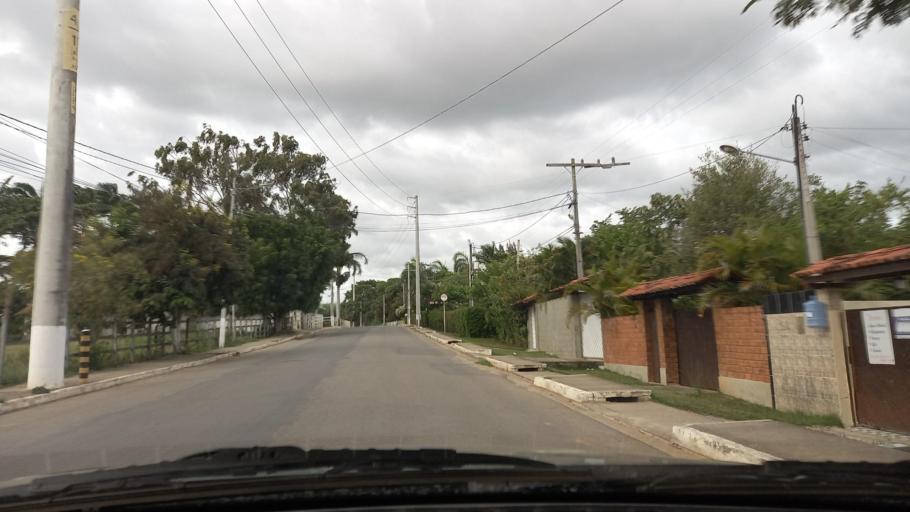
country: BR
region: Pernambuco
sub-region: Gravata
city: Gravata
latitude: -8.2067
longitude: -35.5567
